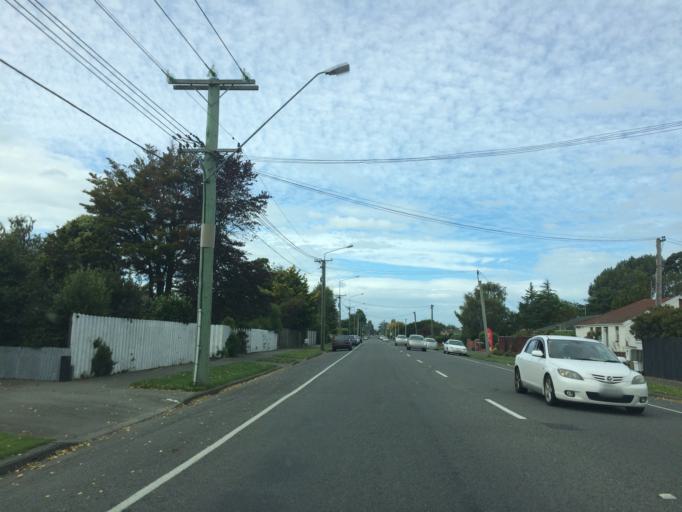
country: NZ
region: Canterbury
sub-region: Christchurch City
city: Christchurch
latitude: -43.5670
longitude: 172.6000
